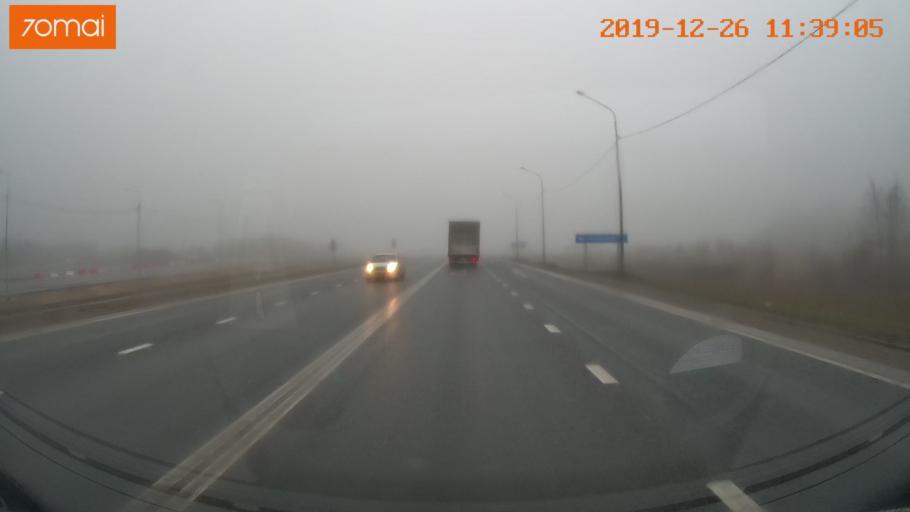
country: RU
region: Vologda
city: Sheksna
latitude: 59.2108
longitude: 38.6067
